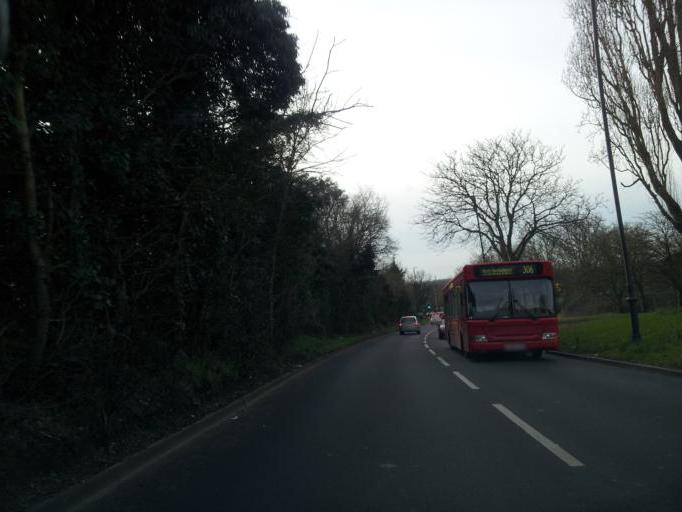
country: GB
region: England
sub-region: Hertfordshire
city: Elstree
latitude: 51.6438
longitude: -0.3006
